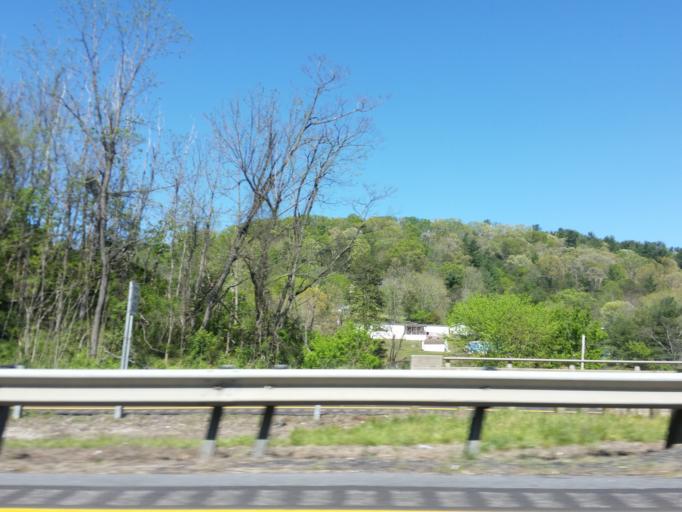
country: US
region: North Carolina
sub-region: Buncombe County
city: Woodfin
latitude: 35.6223
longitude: -82.5748
